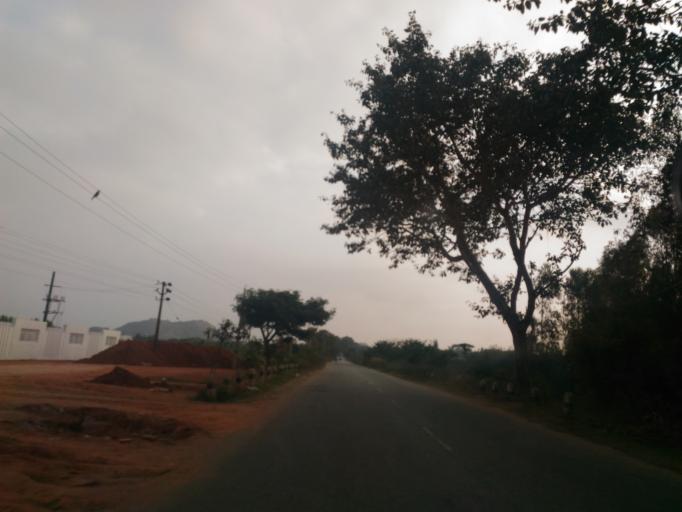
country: IN
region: Karnataka
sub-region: Bangalore Rural
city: Devanhalli
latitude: 13.3208
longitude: 77.6939
